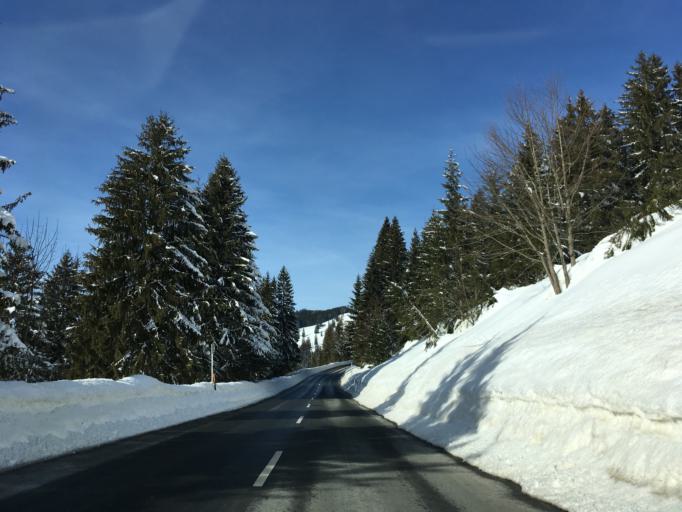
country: DE
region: Bavaria
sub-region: Upper Bavaria
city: Bayrischzell
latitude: 47.6815
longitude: 12.0510
